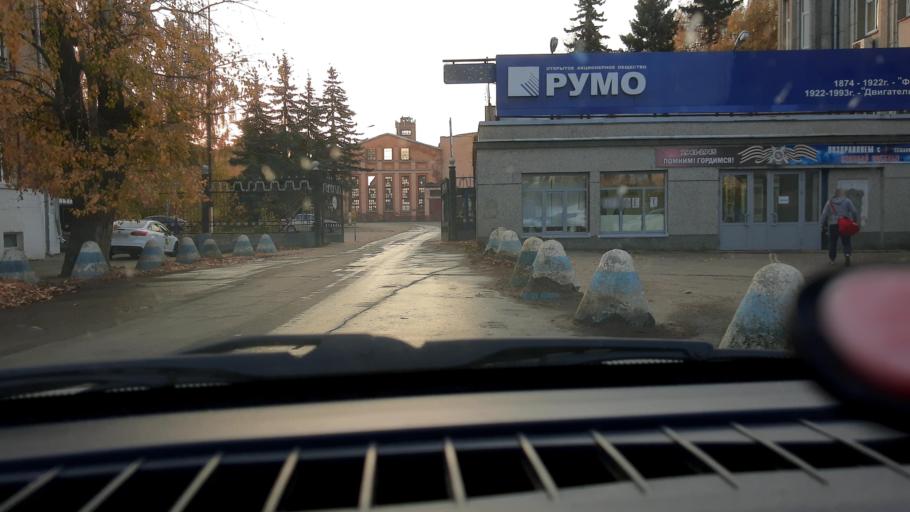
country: RU
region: Nizjnij Novgorod
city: Nizhniy Novgorod
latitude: 56.2652
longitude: 43.9309
